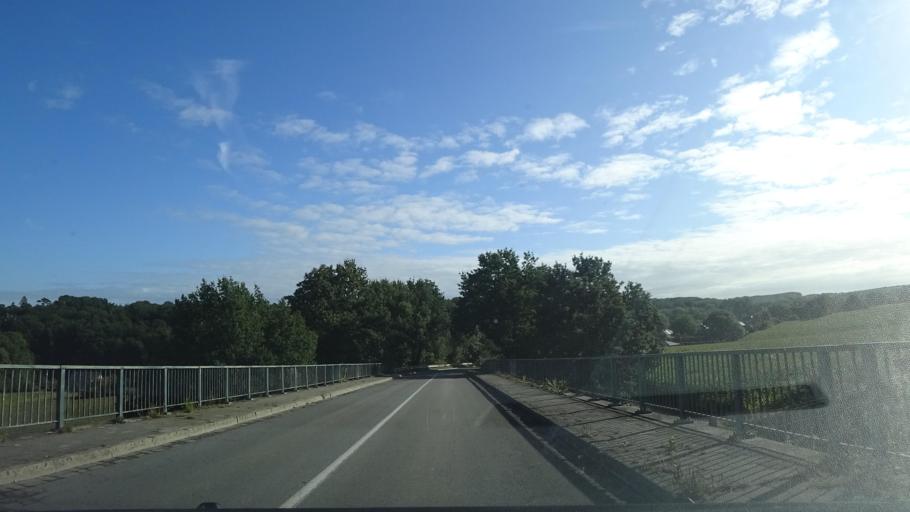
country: BE
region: Wallonia
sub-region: Province du Brabant Wallon
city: Ottignies
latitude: 50.6513
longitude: 4.5897
